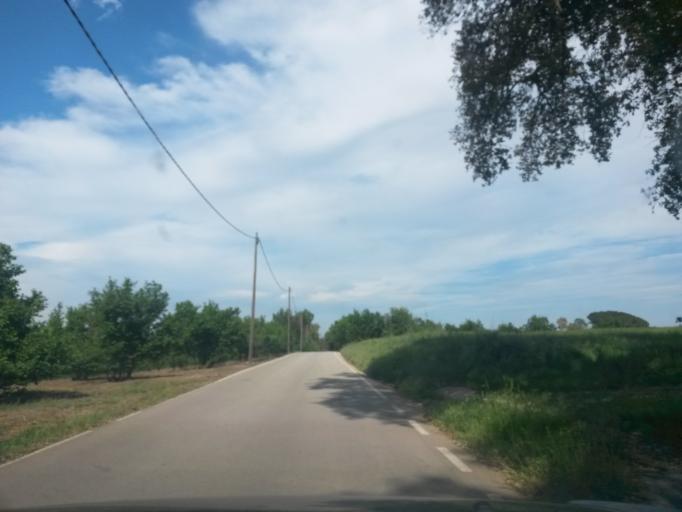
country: ES
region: Catalonia
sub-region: Provincia de Girona
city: Brunyola
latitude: 41.9120
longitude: 2.7087
